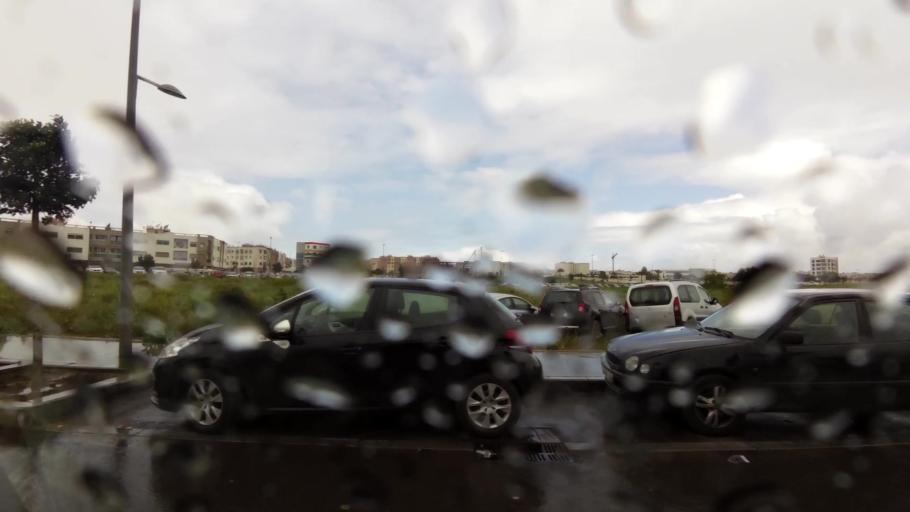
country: MA
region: Grand Casablanca
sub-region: Casablanca
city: Casablanca
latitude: 33.5468
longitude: -7.6687
